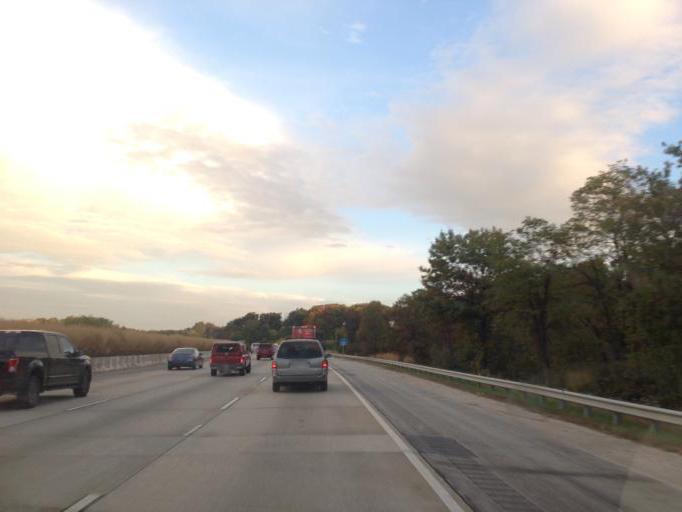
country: US
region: Maryland
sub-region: Baltimore County
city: Garrison
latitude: 39.3816
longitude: -76.7540
